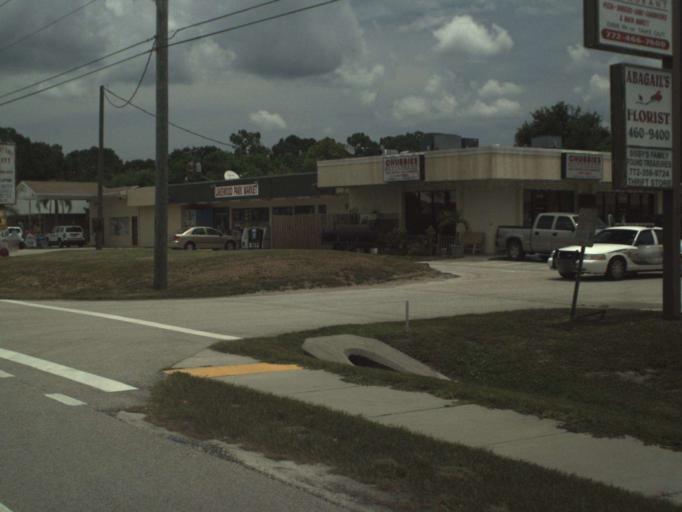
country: US
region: Florida
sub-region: Saint Lucie County
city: Lakewood Park
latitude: 27.5294
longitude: -80.3925
